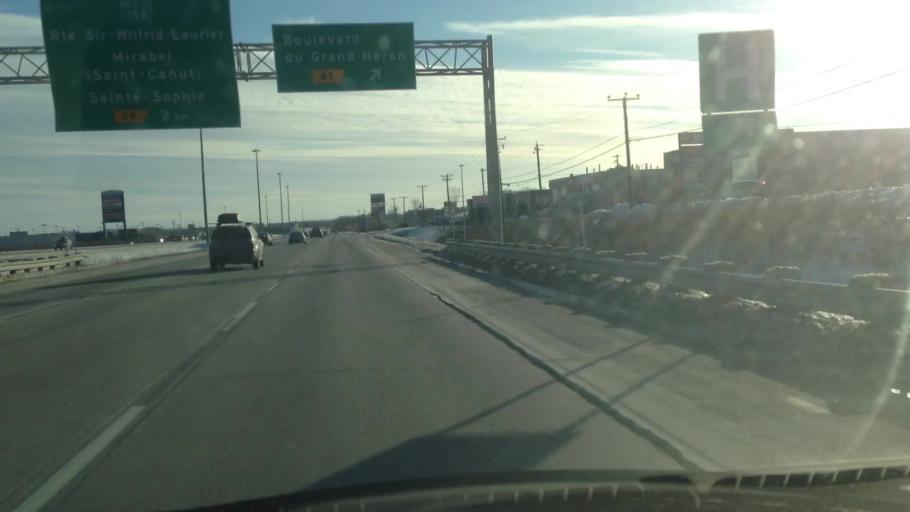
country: CA
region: Quebec
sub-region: Laurentides
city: Saint-Jerome
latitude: 45.7650
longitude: -74.0209
